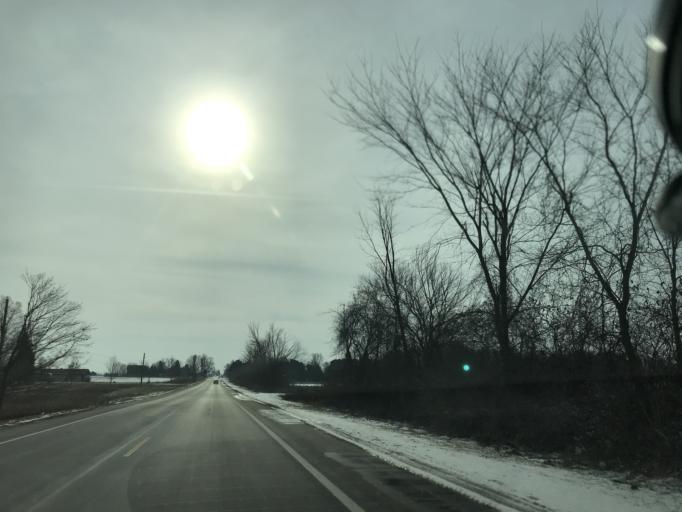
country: US
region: Michigan
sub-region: Ionia County
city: Lake Odessa
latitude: 42.7789
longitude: -85.0743
